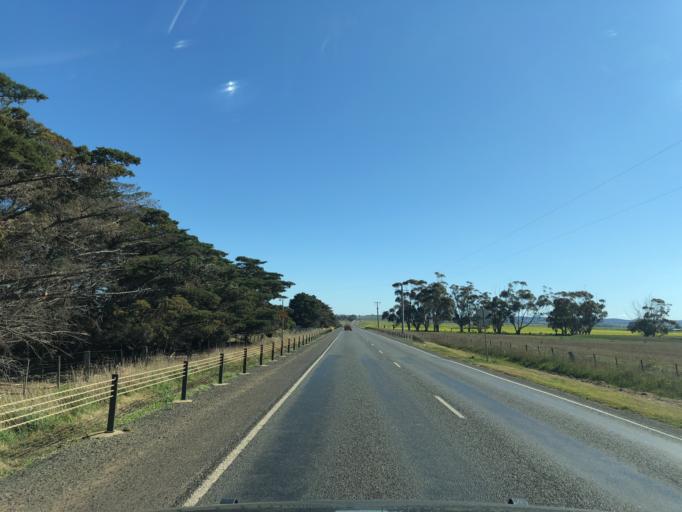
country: AU
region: Victoria
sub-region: Hume
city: Diggers Rest
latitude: -37.6281
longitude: 144.6965
